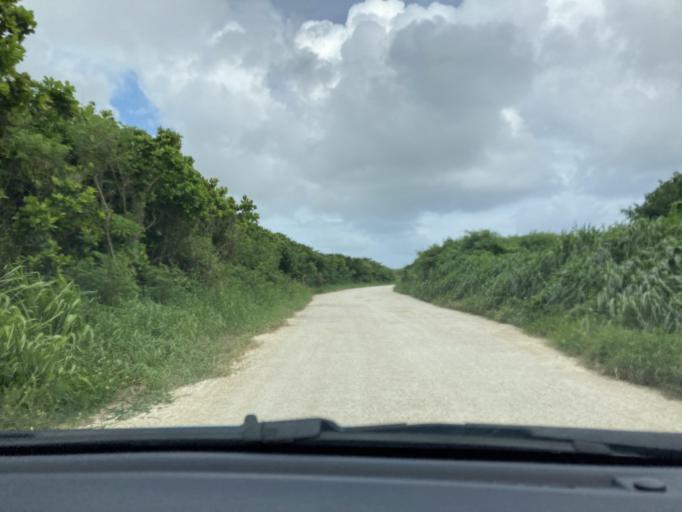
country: JP
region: Okinawa
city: Itoman
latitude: 26.0819
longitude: 127.6851
